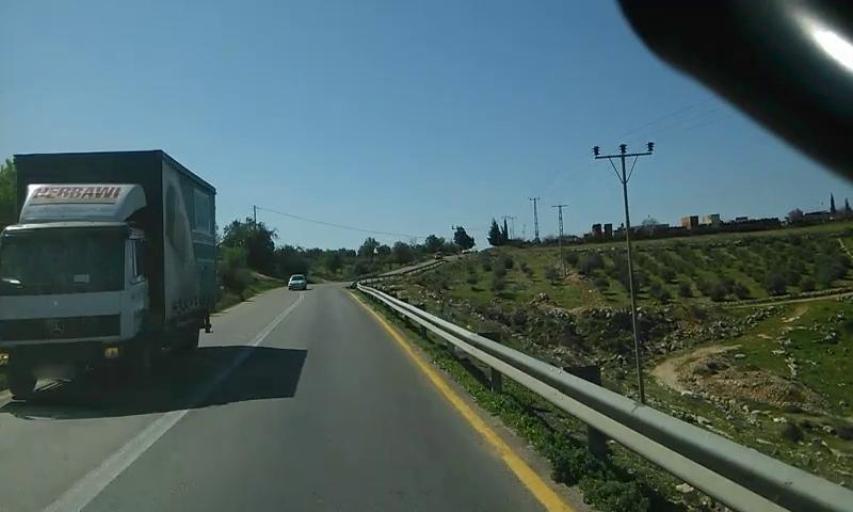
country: PS
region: West Bank
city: Marah Rabbah
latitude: 31.6473
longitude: 35.2032
